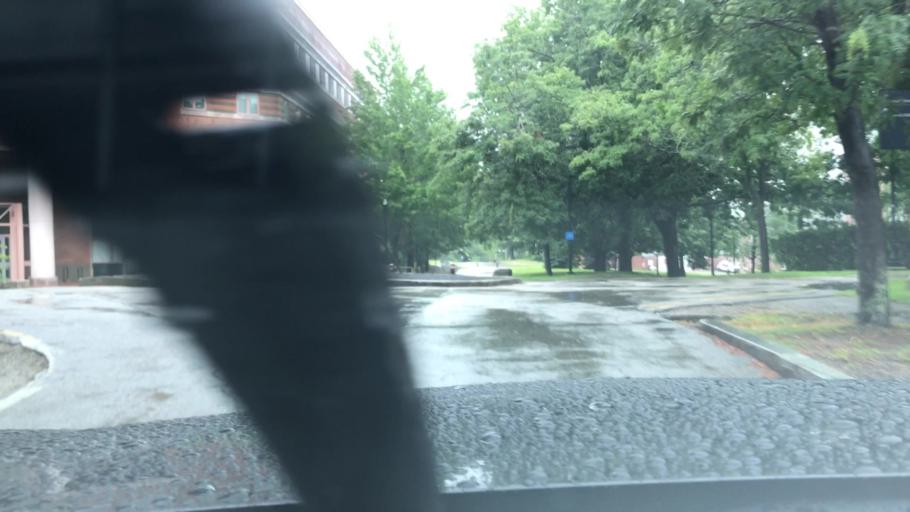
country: US
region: New Hampshire
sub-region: Strafford County
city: Durham
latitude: 43.1349
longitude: -70.9349
